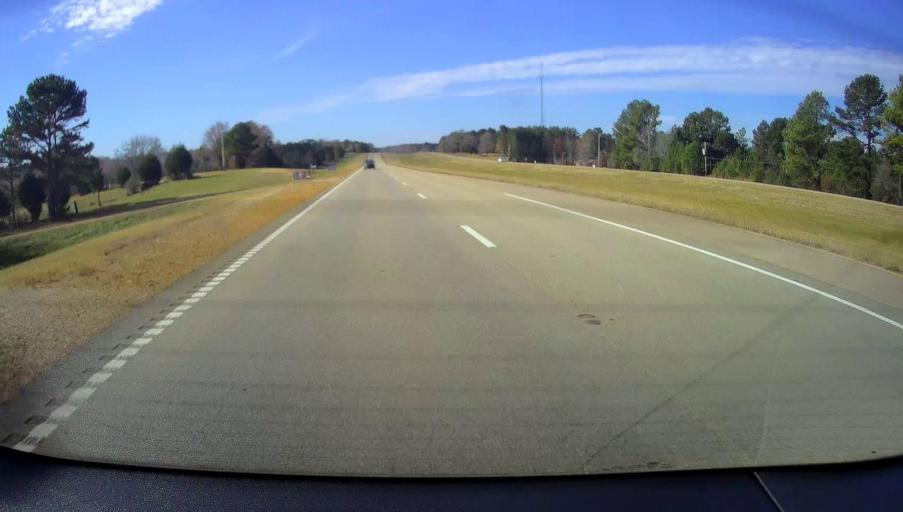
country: US
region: Mississippi
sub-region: Benton County
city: Ashland
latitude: 34.9531
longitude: -89.0102
